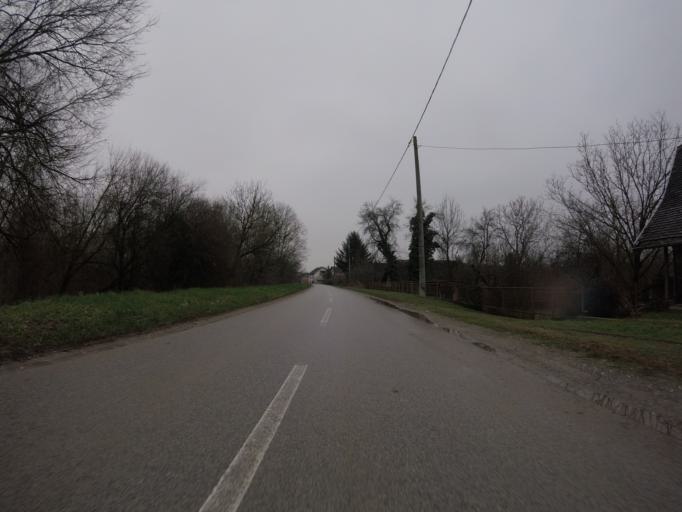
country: HR
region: Sisacko-Moslavacka
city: Lekenik
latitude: 45.6160
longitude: 16.3313
